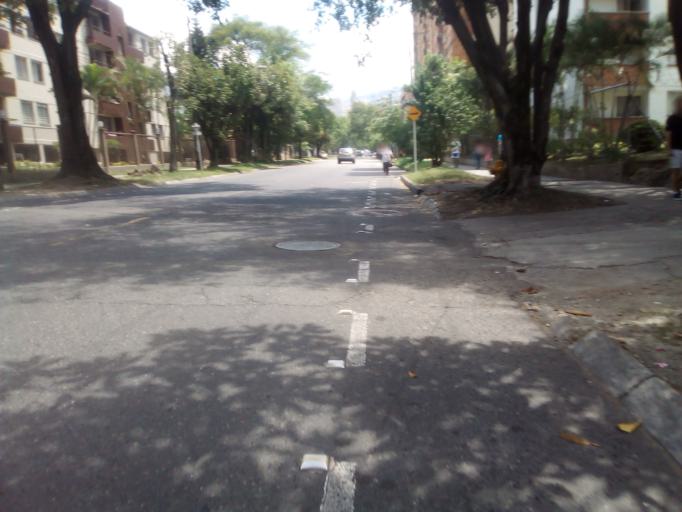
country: CO
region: Antioquia
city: Medellin
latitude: 6.2633
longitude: -75.5891
